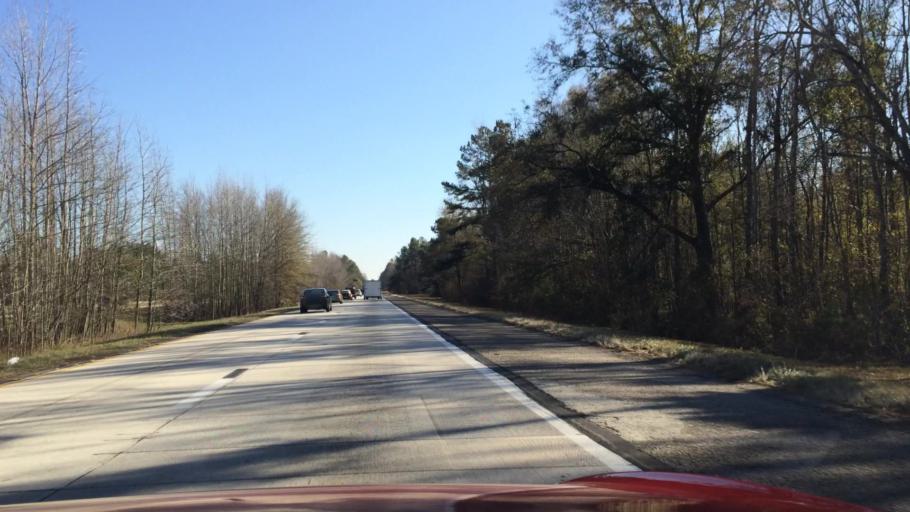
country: US
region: South Carolina
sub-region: Orangeburg County
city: Holly Hill
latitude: 33.2612
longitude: -80.4778
